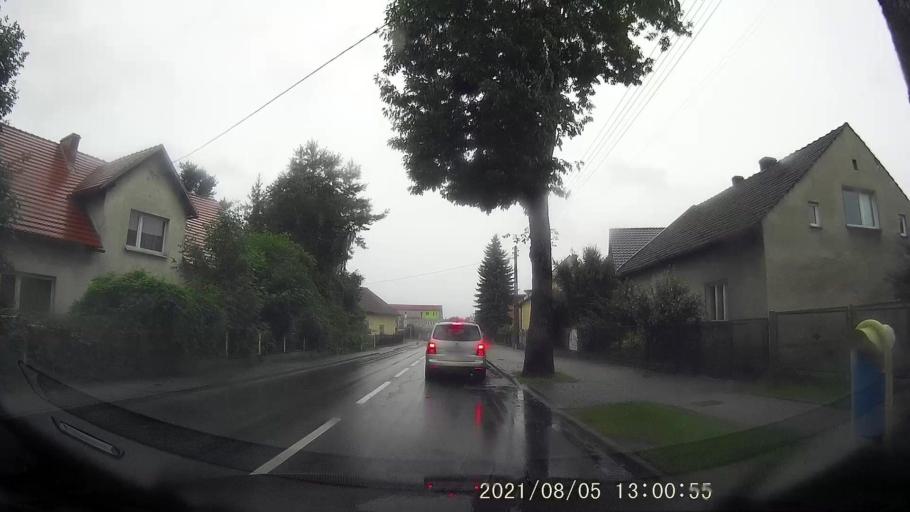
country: PL
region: Opole Voivodeship
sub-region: Powiat krapkowicki
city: Krapkowice
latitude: 50.4821
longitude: 17.9777
